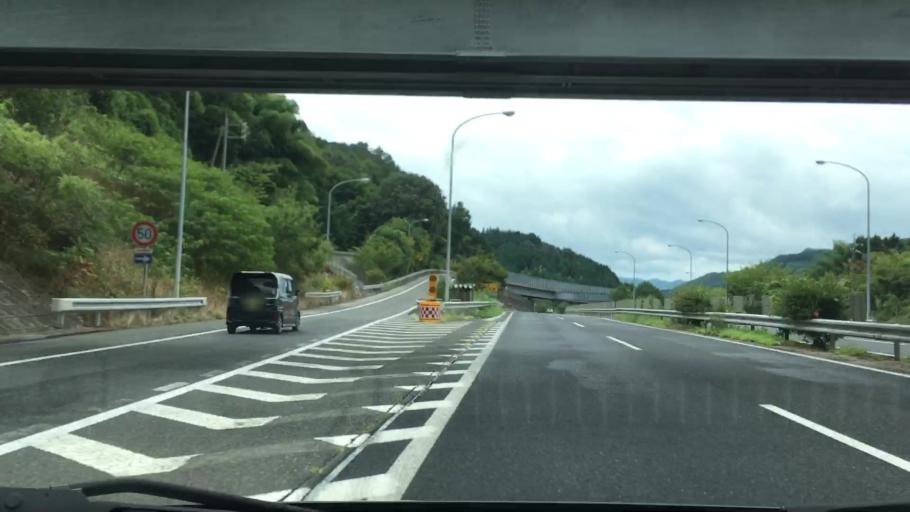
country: JP
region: Okayama
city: Tsuyama
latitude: 35.0532
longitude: 133.8107
